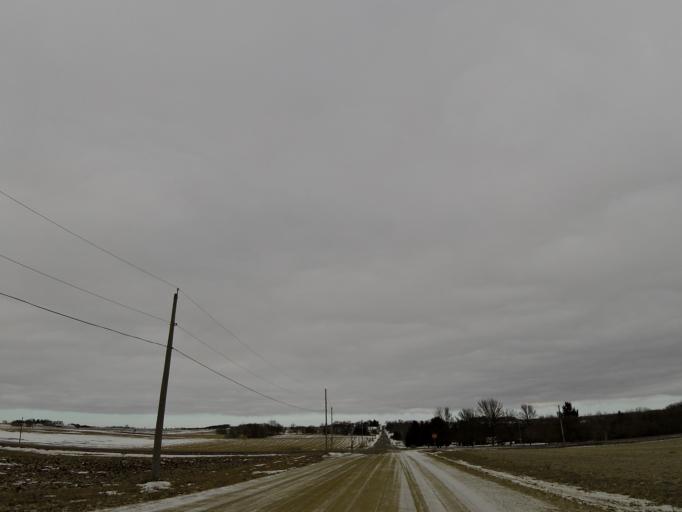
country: US
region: Minnesota
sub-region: Dakota County
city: Hastings
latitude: 44.8179
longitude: -92.8415
